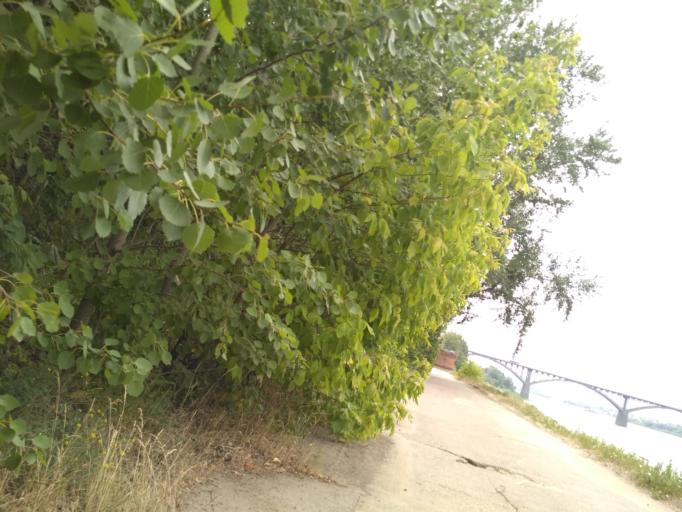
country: RU
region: Nizjnij Novgorod
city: Nizhniy Novgorod
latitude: 56.3070
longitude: 43.9680
